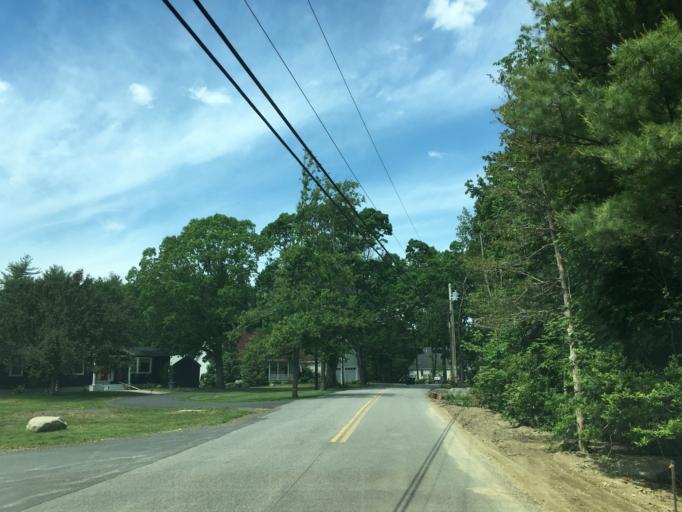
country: US
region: New Hampshire
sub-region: Rockingham County
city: Stratham Station
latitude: 43.0335
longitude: -70.8712
